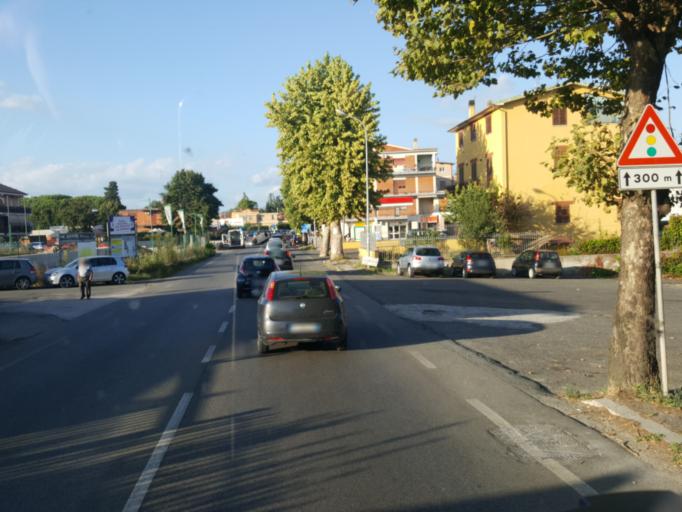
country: IT
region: Latium
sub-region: Citta metropolitana di Roma Capitale
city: Bivio di Capanelle
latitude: 42.1191
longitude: 12.5898
